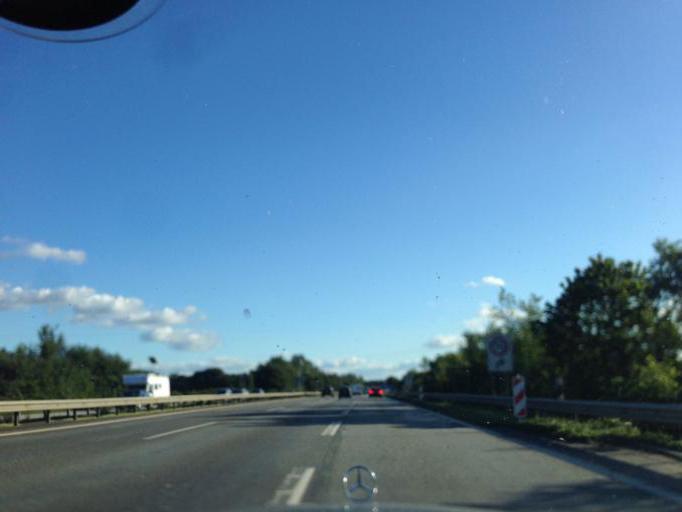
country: DE
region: Schleswig-Holstein
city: Padenstedt
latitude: 54.0437
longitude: 9.9295
